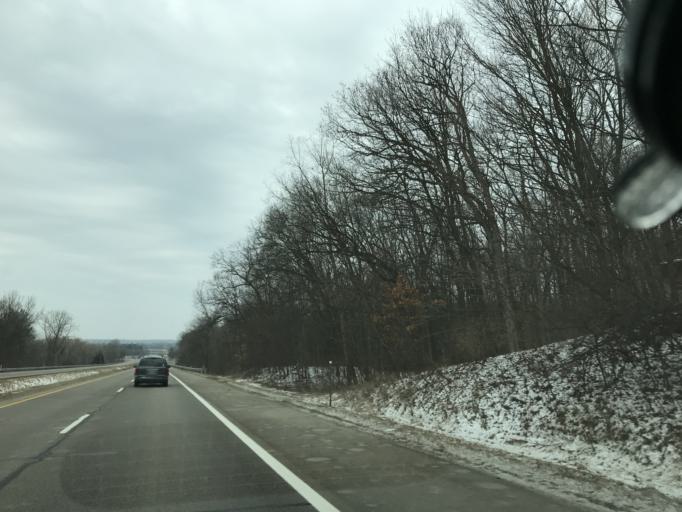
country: US
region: Michigan
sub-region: Kent County
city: Rockford
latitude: 43.0801
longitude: -85.5636
